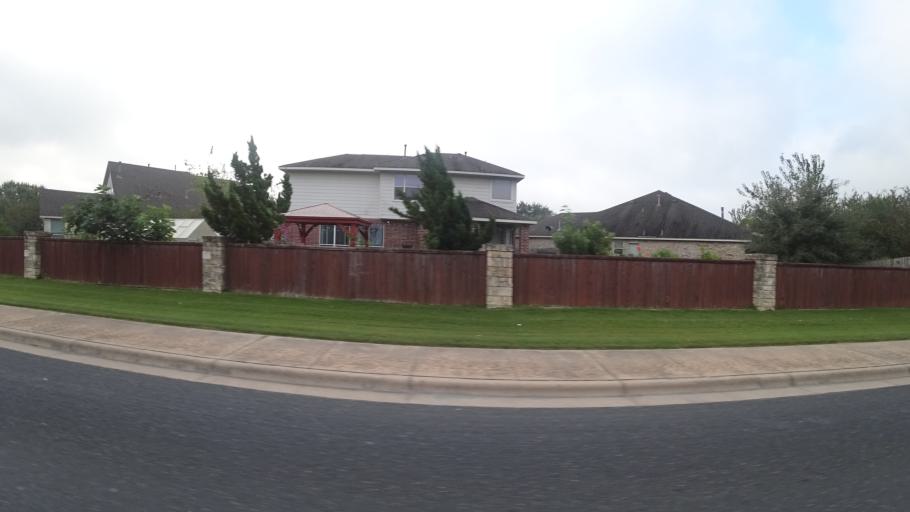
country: US
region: Texas
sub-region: Travis County
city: Wells Branch
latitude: 30.3741
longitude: -97.6623
